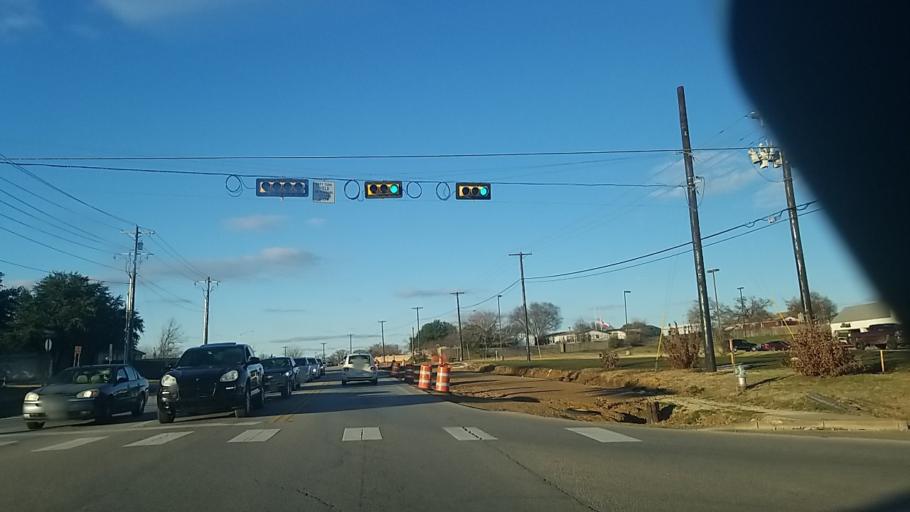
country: US
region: Texas
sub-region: Denton County
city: Corinth
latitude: 33.1583
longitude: -97.1056
